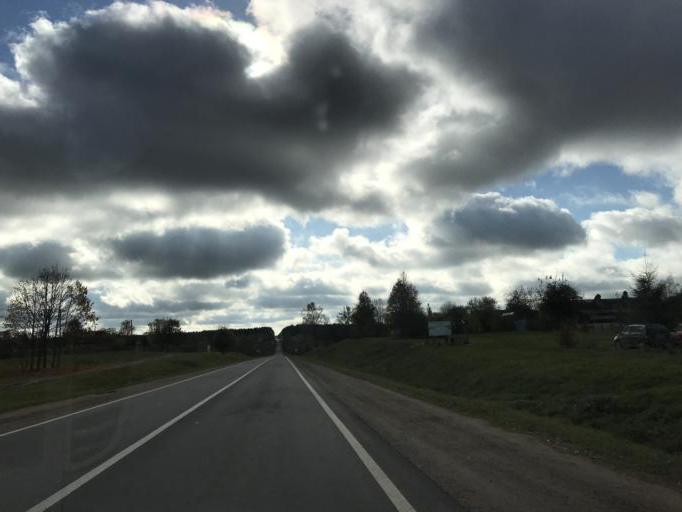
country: BY
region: Mogilev
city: Bykhaw
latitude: 53.3925
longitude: 30.3925
